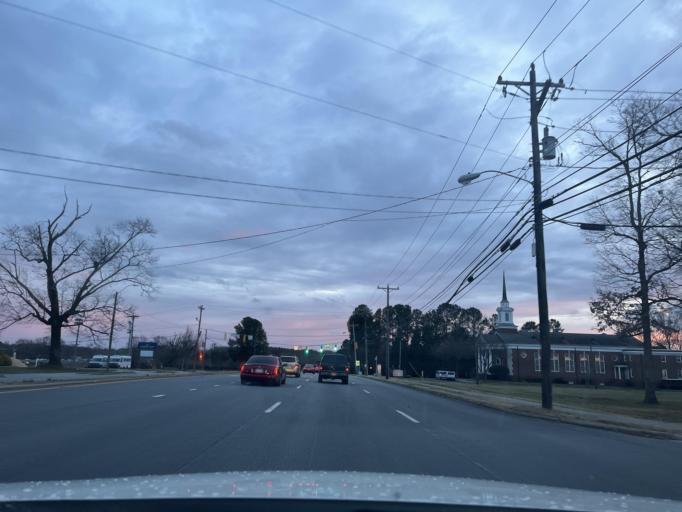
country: US
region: North Carolina
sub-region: Guilford County
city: Greensboro
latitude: 36.0371
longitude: -79.8499
